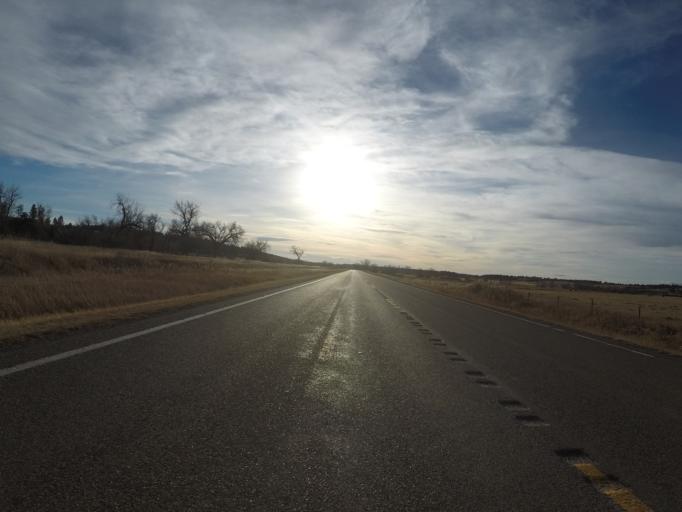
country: US
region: Montana
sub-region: Musselshell County
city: Roundup
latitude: 46.3499
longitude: -108.6764
